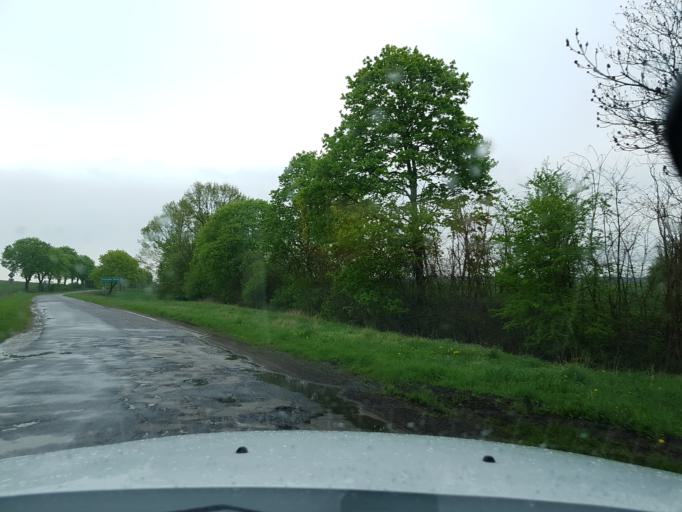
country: PL
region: West Pomeranian Voivodeship
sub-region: Powiat mysliborski
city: Debno
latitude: 52.8544
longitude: 14.6765
